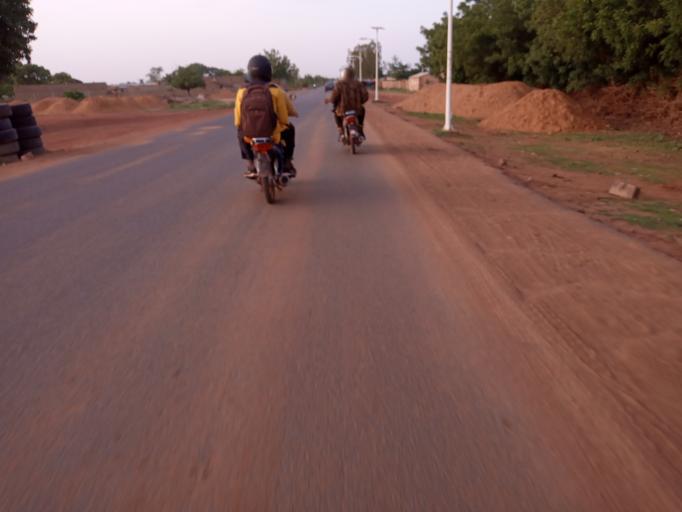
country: ML
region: Bamako
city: Bamako
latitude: 12.3072
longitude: -8.1549
